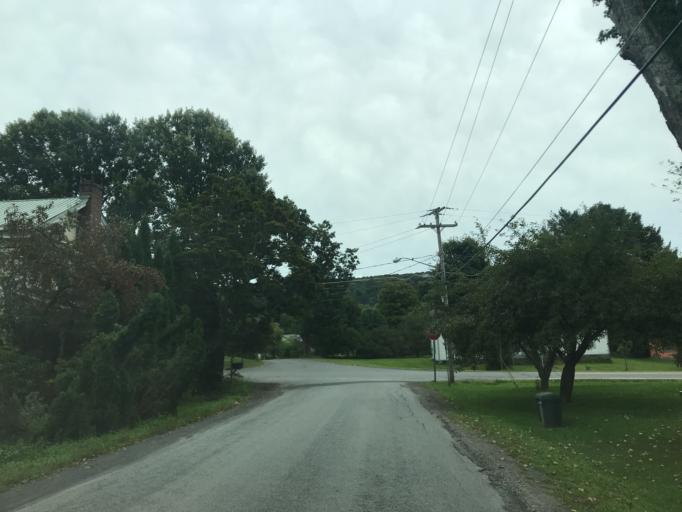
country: US
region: New York
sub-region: Otsego County
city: Worcester
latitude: 42.5455
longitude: -74.6650
